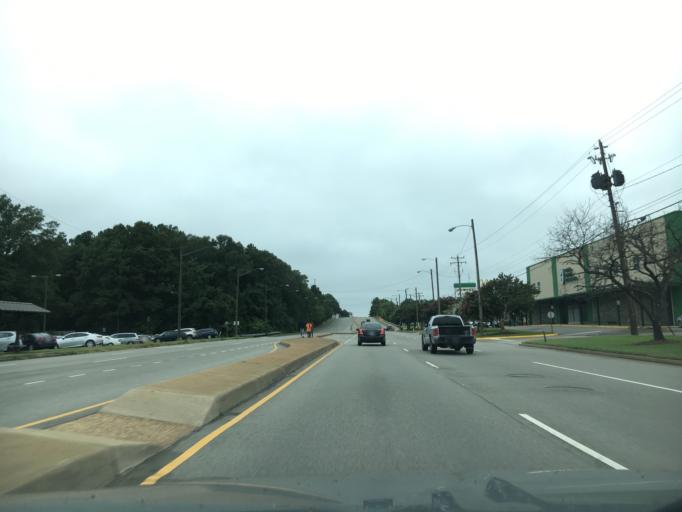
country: US
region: Virginia
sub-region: City of Richmond
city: Richmond
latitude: 37.5018
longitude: -77.4742
